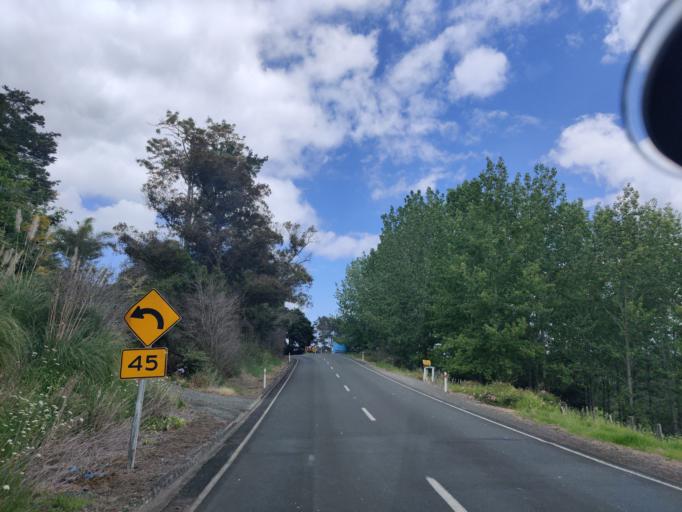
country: NZ
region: Northland
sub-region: Far North District
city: Kaitaia
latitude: -35.2845
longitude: 173.4842
